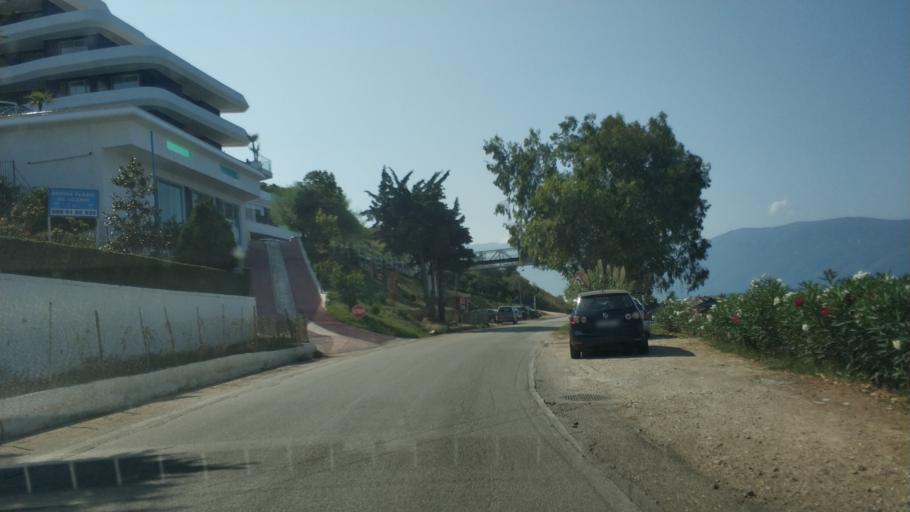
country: AL
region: Vlore
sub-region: Rrethi i Vlores
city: Orikum
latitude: 40.3633
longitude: 19.4806
